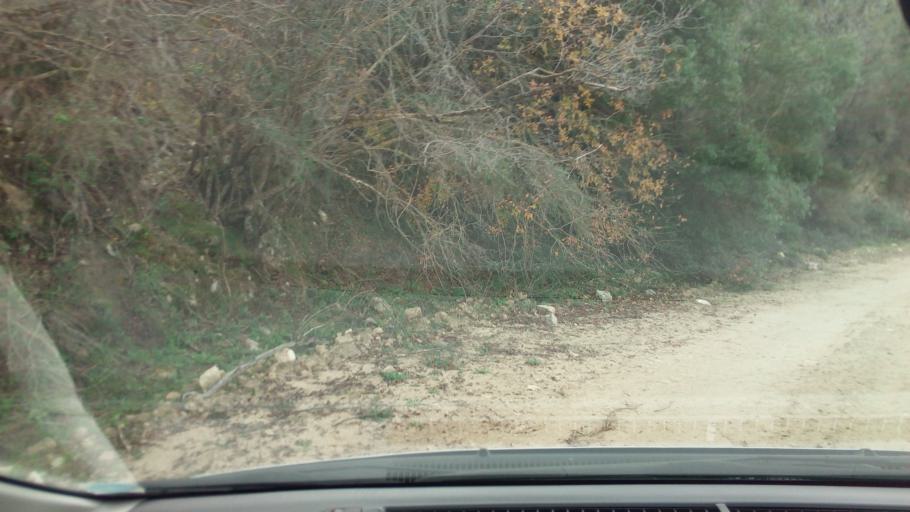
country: CY
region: Pafos
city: Mesogi
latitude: 34.7976
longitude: 32.5455
